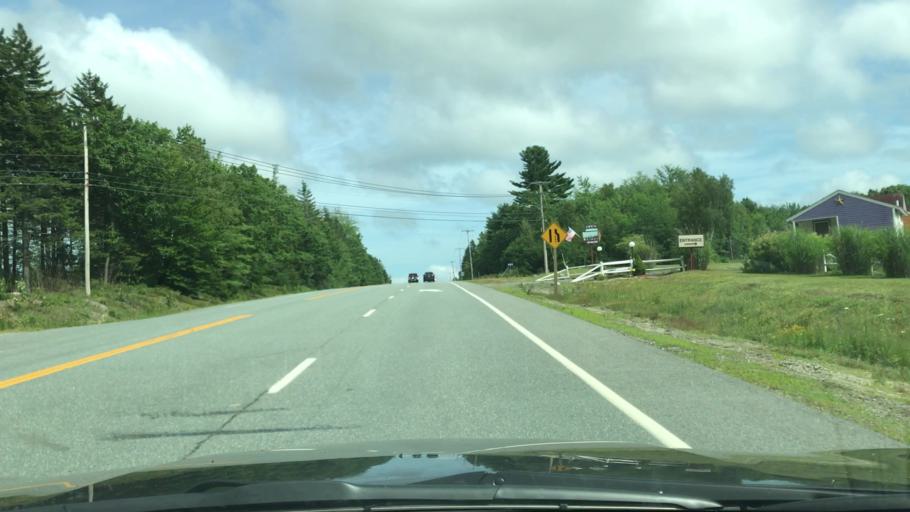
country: US
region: Maine
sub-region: Hancock County
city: Surry
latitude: 44.5543
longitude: -68.5385
